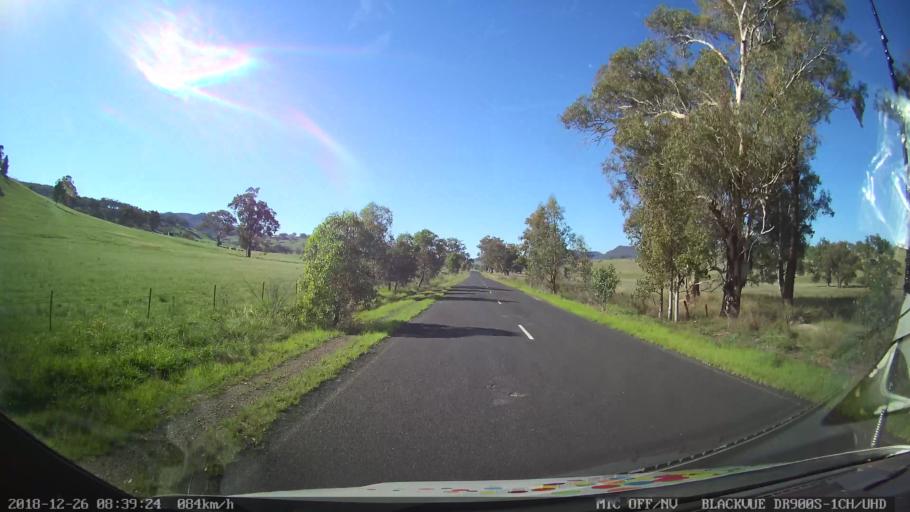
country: AU
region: New South Wales
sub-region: Mid-Western Regional
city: Kandos
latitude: -32.4530
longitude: 150.0757
